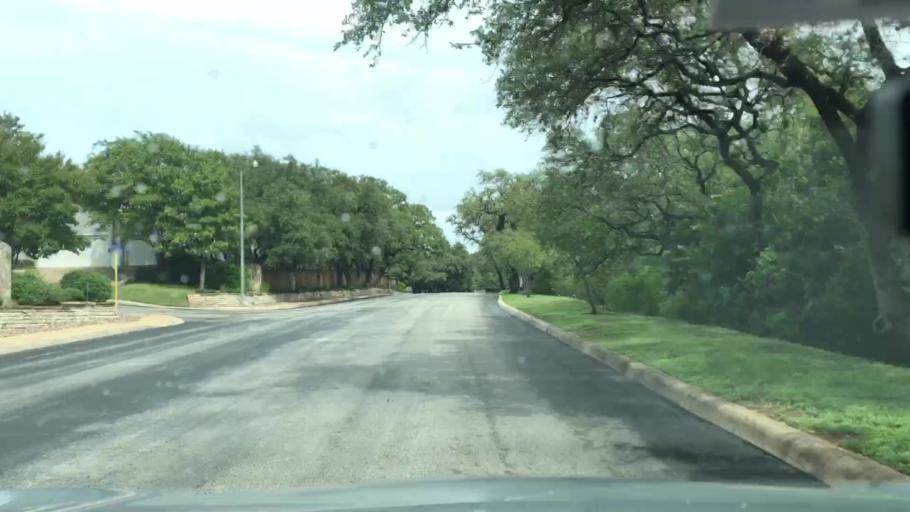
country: US
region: Texas
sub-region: Bexar County
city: Shavano Park
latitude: 29.5989
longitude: -98.5358
